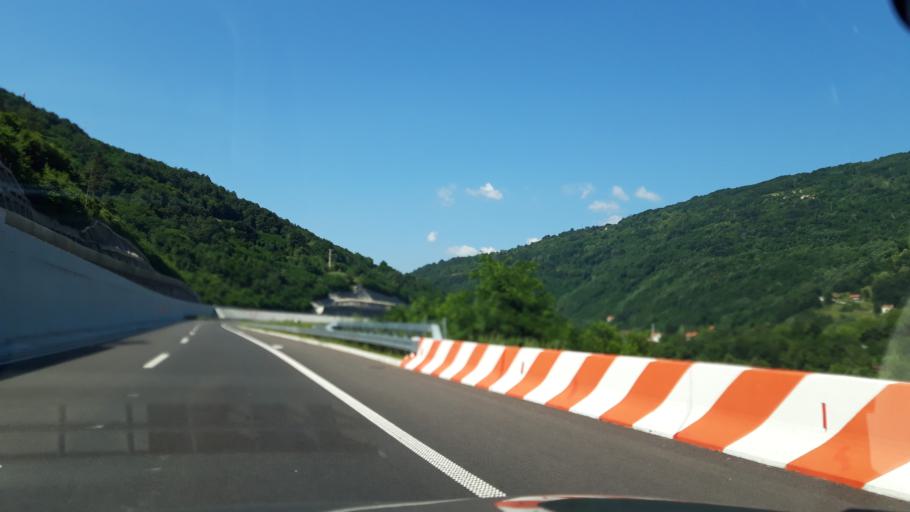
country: RS
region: Central Serbia
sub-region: Pcinjski Okrug
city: Vladicin Han
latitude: 42.7715
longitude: 22.0857
